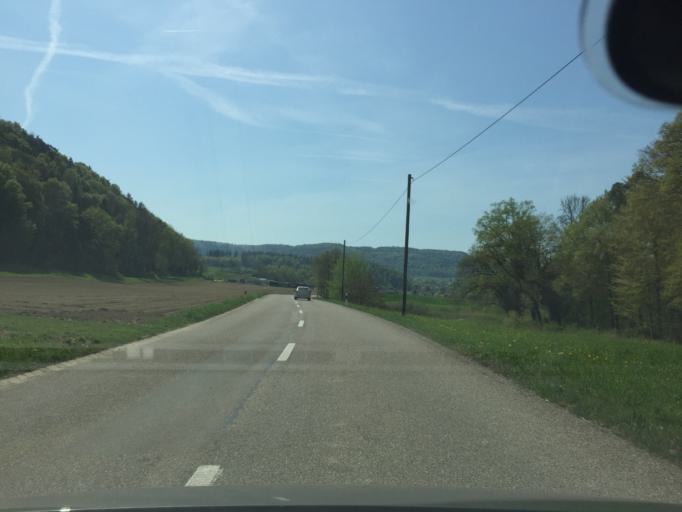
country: CH
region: Zurich
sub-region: Bezirk Andelfingen
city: Marthalen
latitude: 47.5861
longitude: 8.6188
